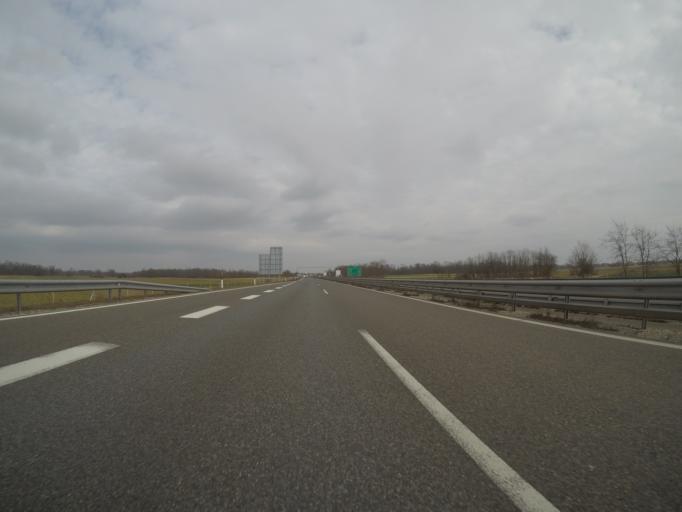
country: SI
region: Murska Sobota
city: Rakican
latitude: 46.6353
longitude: 16.2109
